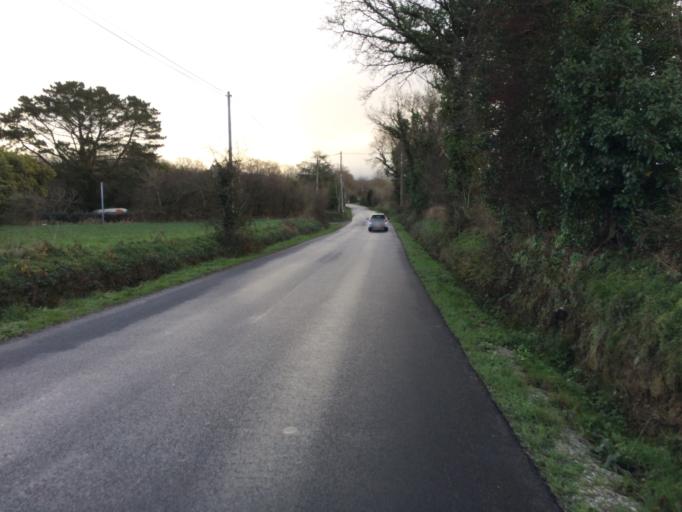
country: FR
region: Brittany
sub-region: Departement du Finistere
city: Daoulas
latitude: 48.3372
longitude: -4.2683
